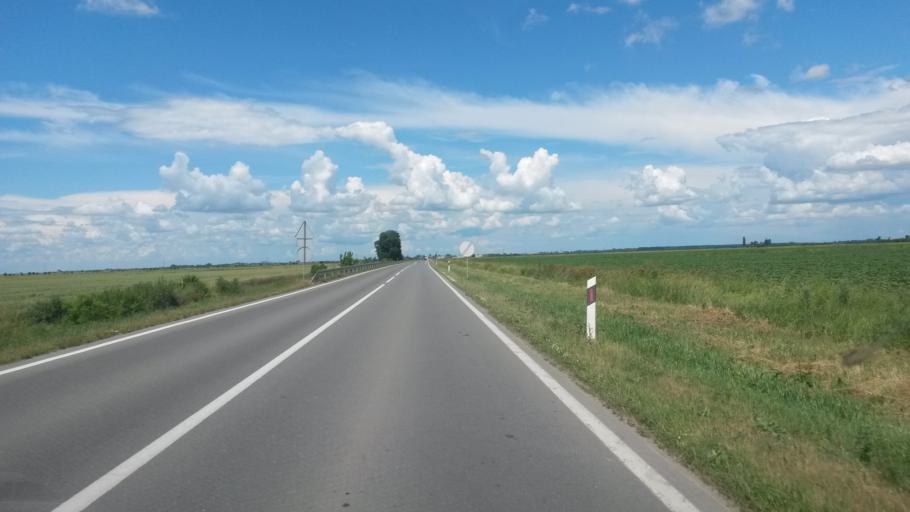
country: HR
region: Osjecko-Baranjska
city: Vladislavci
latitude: 45.4718
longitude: 18.5325
